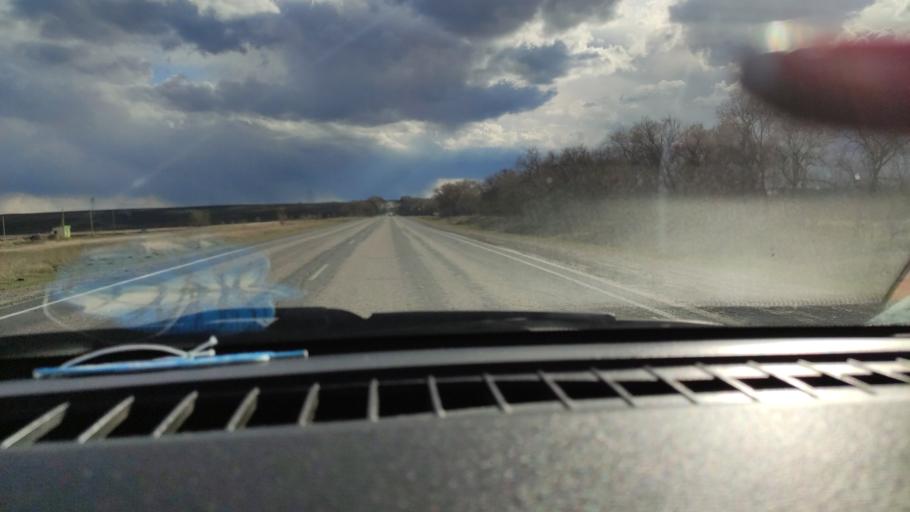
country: RU
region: Saratov
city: Sinodskoye
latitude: 51.9682
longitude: 46.6369
